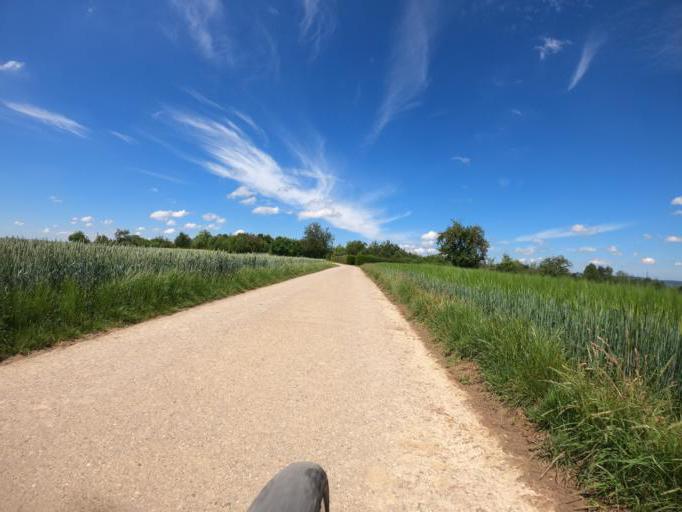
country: DE
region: Baden-Wuerttemberg
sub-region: Regierungsbezirk Stuttgart
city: Tamm
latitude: 48.9159
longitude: 9.1113
